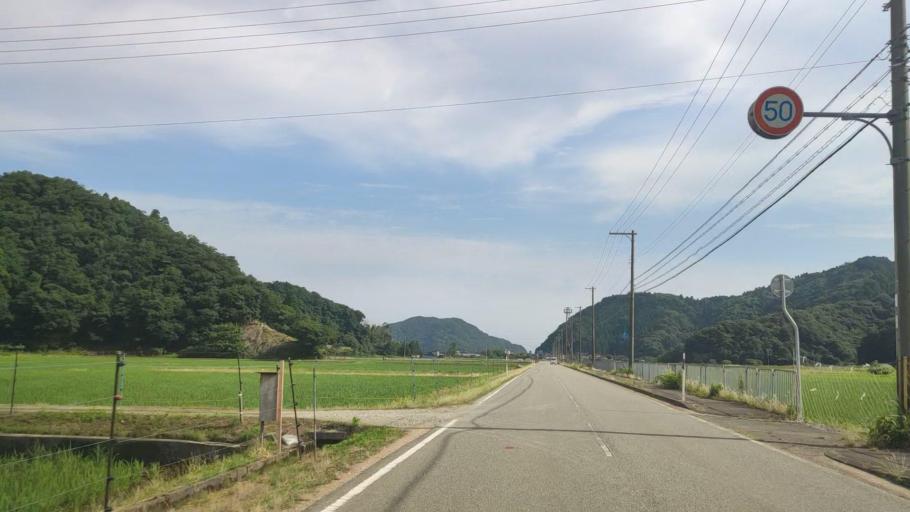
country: JP
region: Hyogo
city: Toyooka
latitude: 35.6275
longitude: 134.8410
